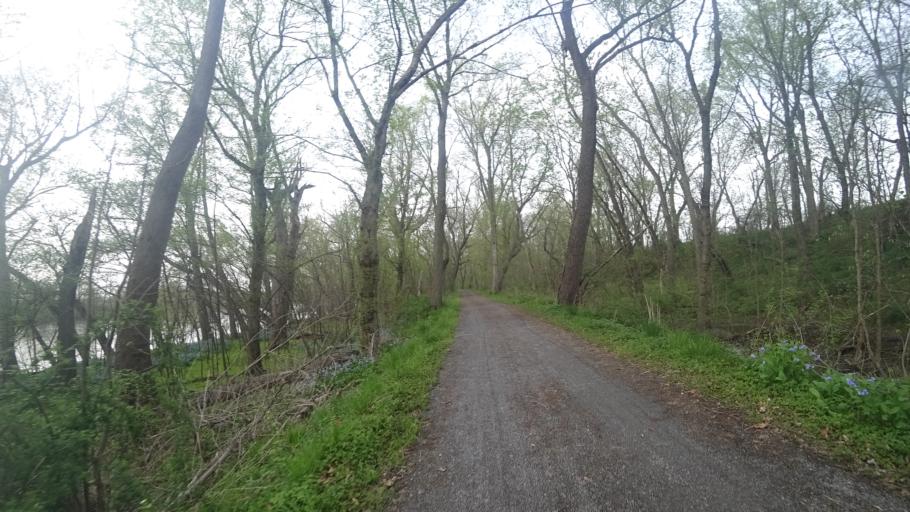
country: US
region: Virginia
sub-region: Loudoun County
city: Leesburg
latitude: 39.1348
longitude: -77.5144
